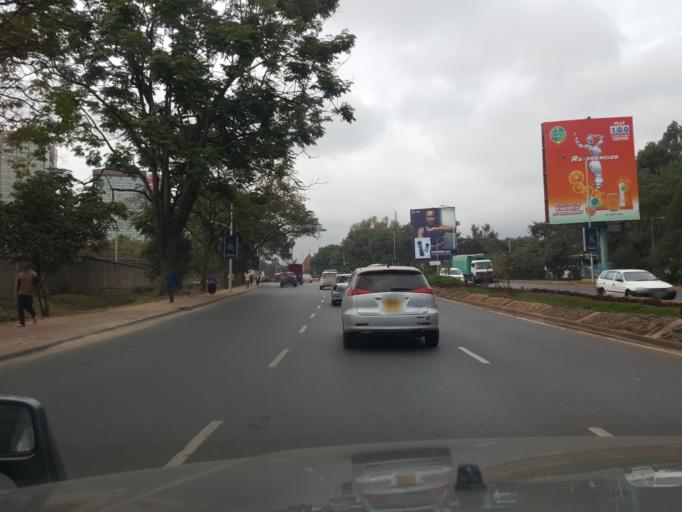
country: KE
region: Nairobi Area
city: Nairobi
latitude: -1.2789
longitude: 36.8140
